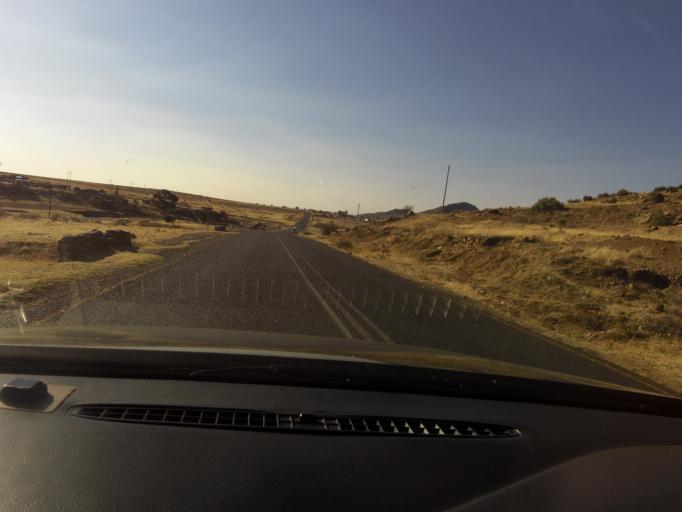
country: LS
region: Mafeteng
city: Mafeteng
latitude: -29.8698
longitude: 27.2373
